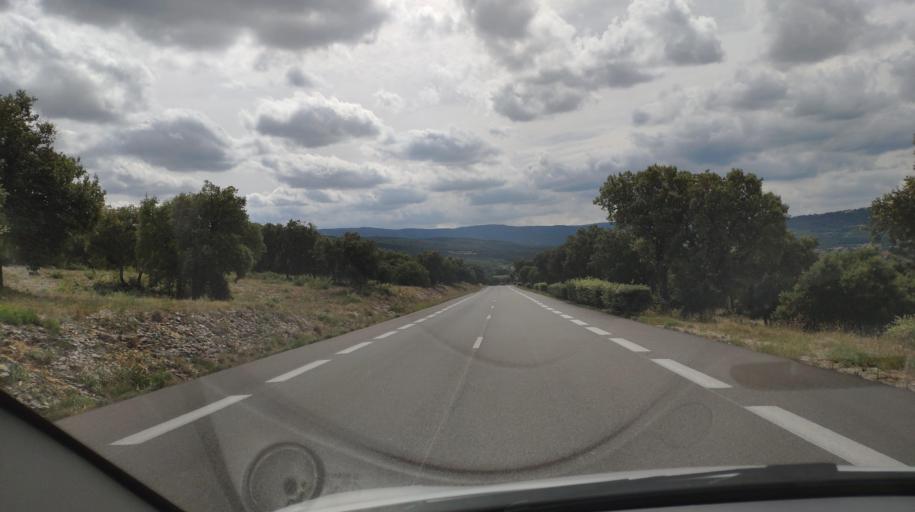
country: FR
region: Provence-Alpes-Cote d'Azur
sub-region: Departement du Vaucluse
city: Villes-sur-Auzon
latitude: 44.0616
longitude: 5.2433
